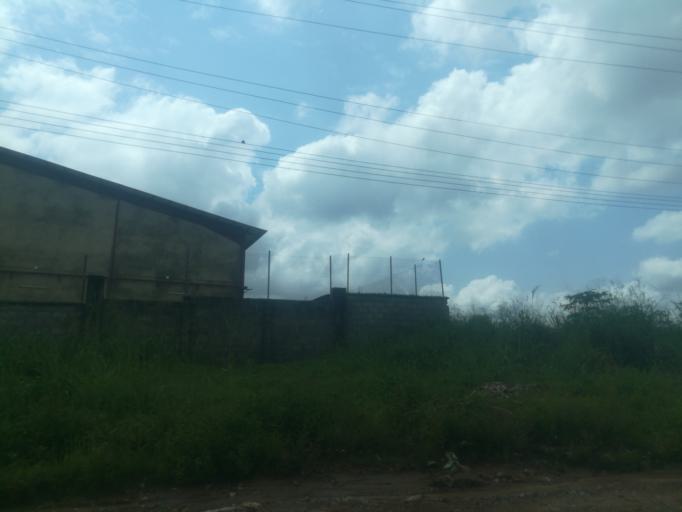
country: NG
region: Oyo
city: Ibadan
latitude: 7.3612
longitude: 3.8443
